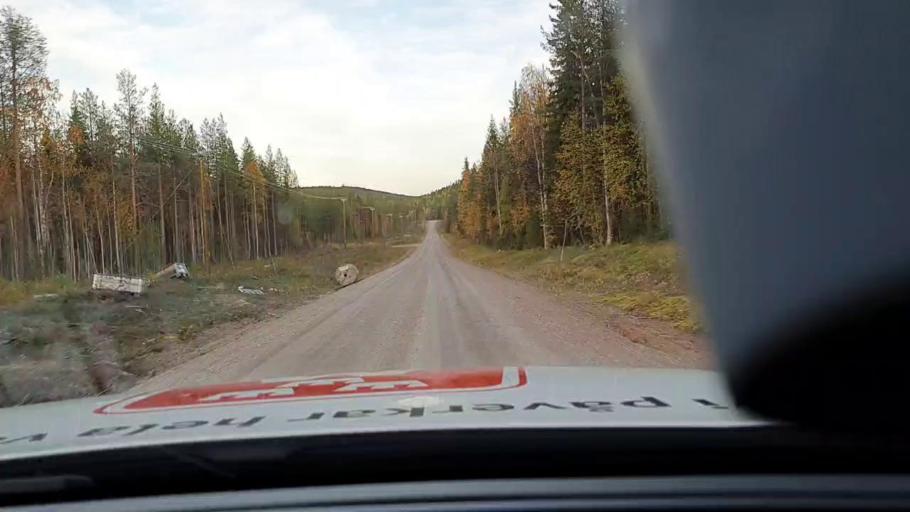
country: SE
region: Norrbotten
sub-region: Overkalix Kommun
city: OEverkalix
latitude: 66.3272
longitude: 22.5990
